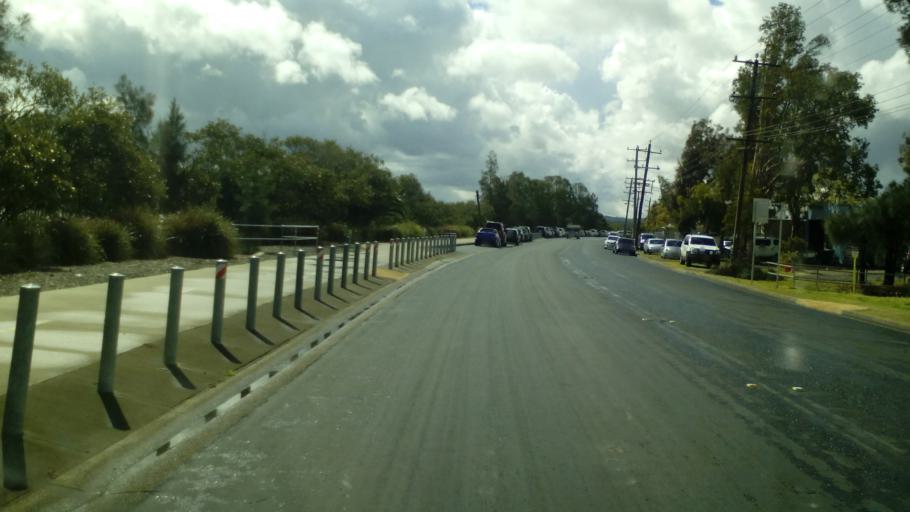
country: AU
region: New South Wales
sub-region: Lake Macquarie Shire
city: Glendale
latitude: -32.9555
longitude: 151.6150
